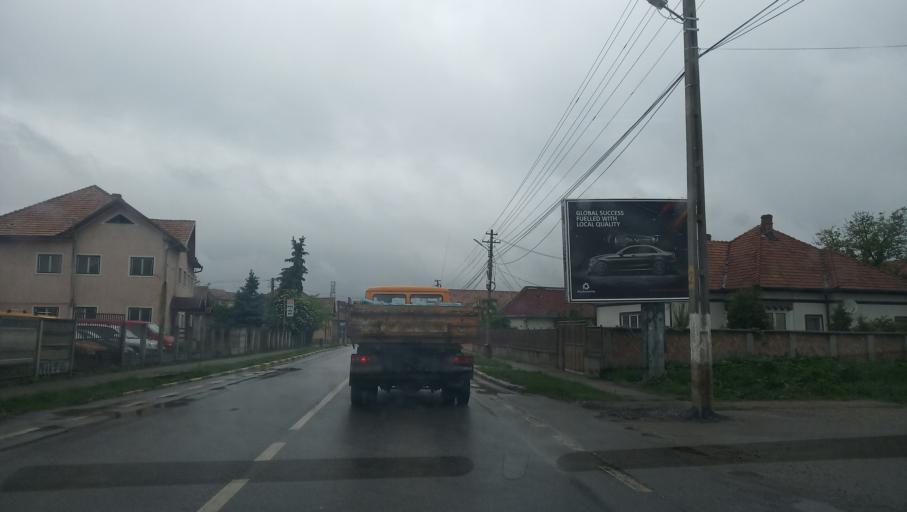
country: RO
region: Alba
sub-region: Municipiul Sebes
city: Sebes
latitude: 45.9531
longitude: 23.5804
